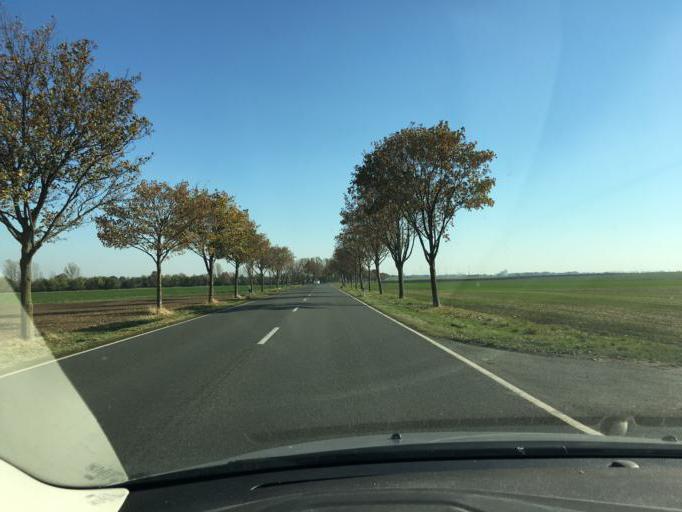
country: DE
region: Saxony-Anhalt
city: Wanzleben
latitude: 52.0297
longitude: 11.4820
